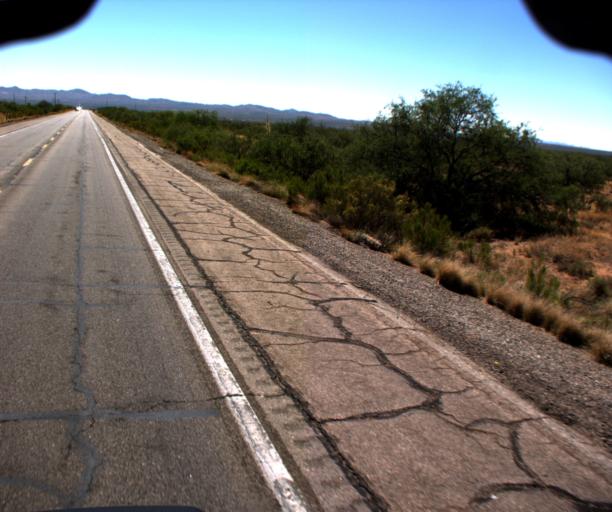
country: US
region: Arizona
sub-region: Pinal County
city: Oracle
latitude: 32.6027
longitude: -110.8664
